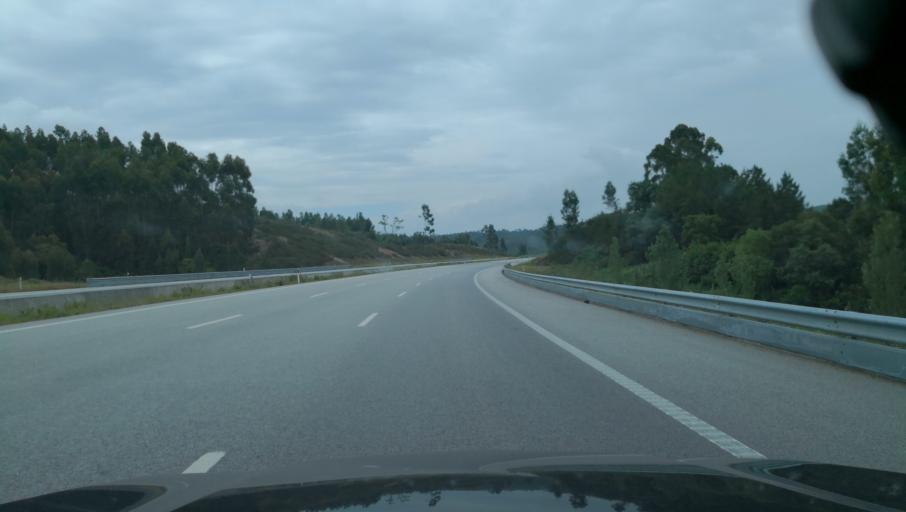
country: PT
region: Coimbra
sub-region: Montemor-O-Velho
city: Montemor-o-Velho
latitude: 40.1329
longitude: -8.7442
